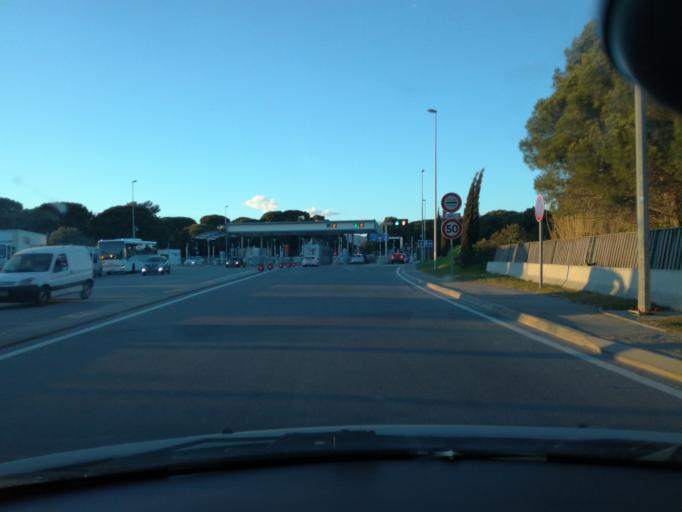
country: FR
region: Provence-Alpes-Cote d'Azur
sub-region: Departement du Var
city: Puget-sur-Argens
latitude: 43.4561
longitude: 6.6900
